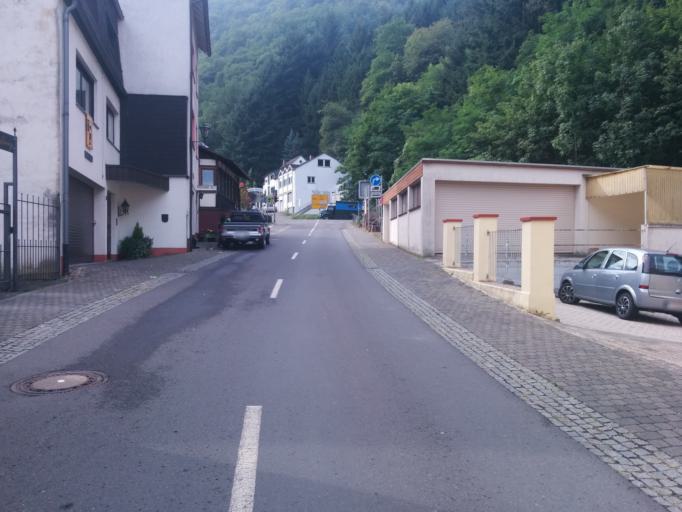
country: DE
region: Rheinland-Pfalz
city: Bernkastel-Kues
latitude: 49.9113
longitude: 7.0781
